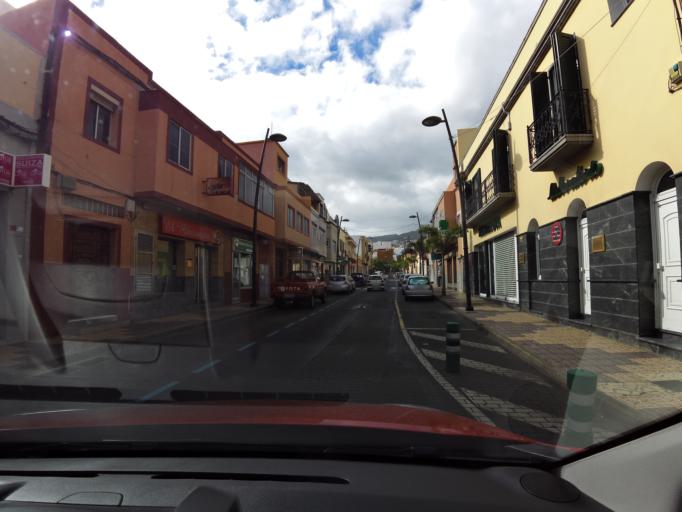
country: ES
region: Canary Islands
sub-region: Provincia de Las Palmas
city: Ingenio
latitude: 27.9198
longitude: -15.4372
